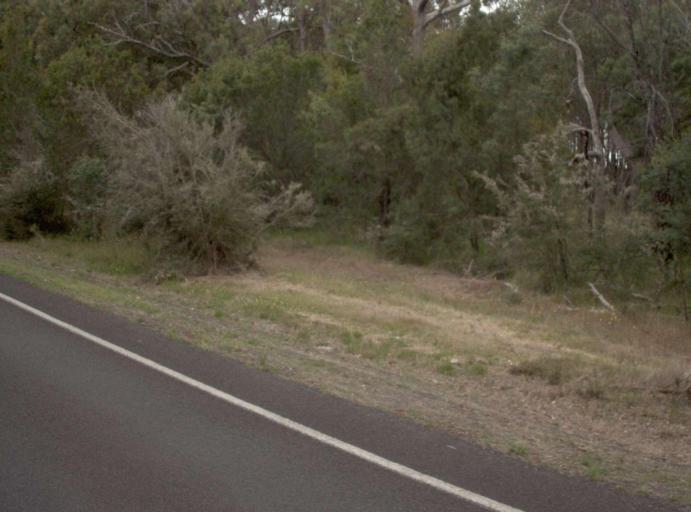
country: AU
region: Victoria
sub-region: Wellington
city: Sale
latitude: -38.3594
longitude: 146.9932
